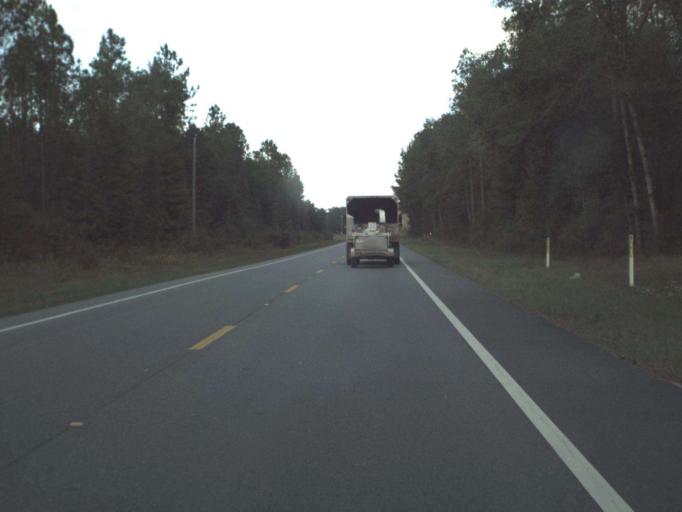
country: US
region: Florida
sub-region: Holmes County
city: Bonifay
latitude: 30.6727
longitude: -85.6414
